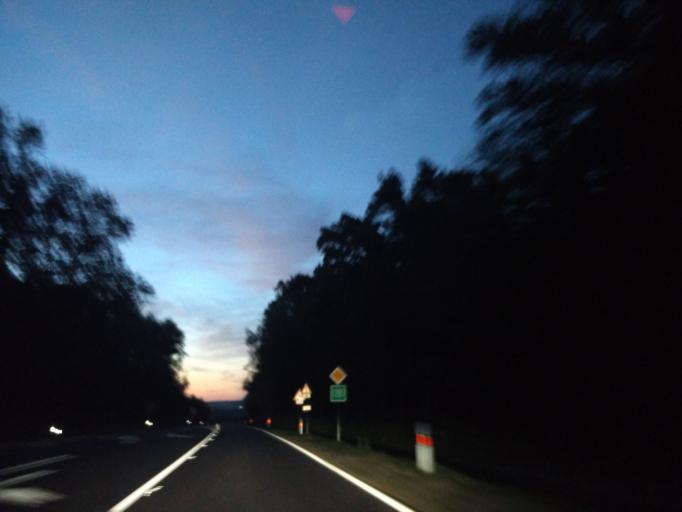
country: HU
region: Zala
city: Zalaegerszeg
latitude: 46.9088
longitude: 16.8589
